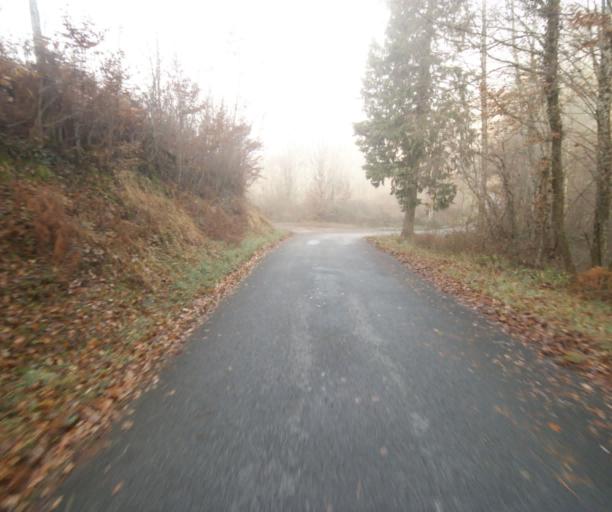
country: FR
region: Limousin
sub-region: Departement de la Correze
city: Laguenne
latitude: 45.2599
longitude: 1.7892
